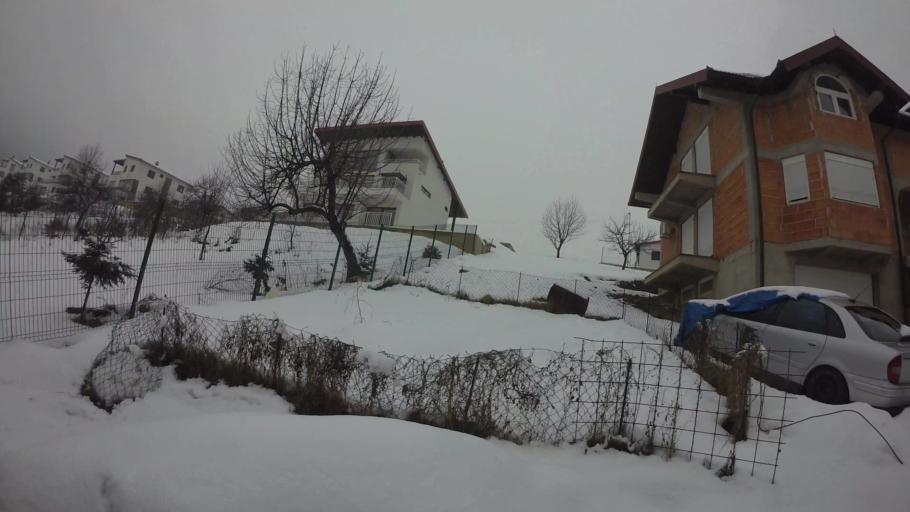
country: BA
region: Federation of Bosnia and Herzegovina
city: Hadzici
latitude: 43.8441
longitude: 18.2627
